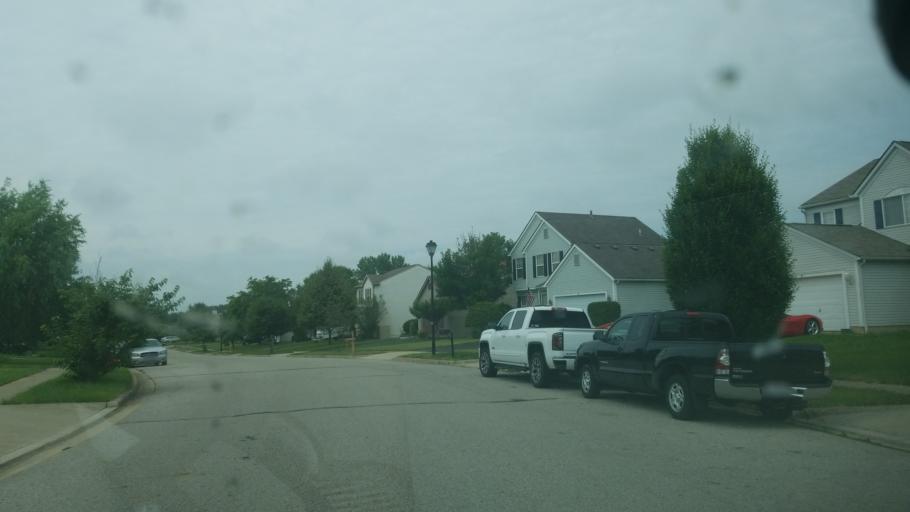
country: US
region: Ohio
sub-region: Franklin County
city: Reynoldsburg
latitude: 40.0071
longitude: -82.7677
